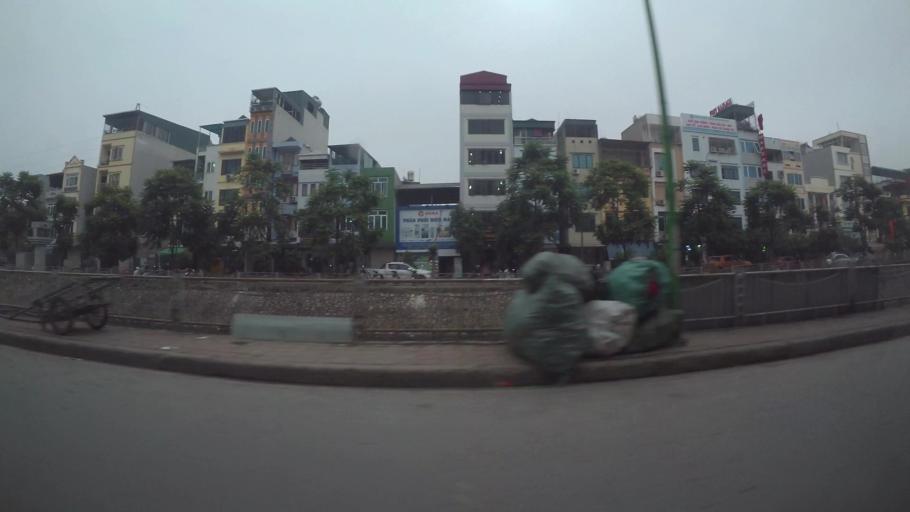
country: VN
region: Ha Noi
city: Hai BaTrung
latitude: 20.9933
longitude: 105.8365
